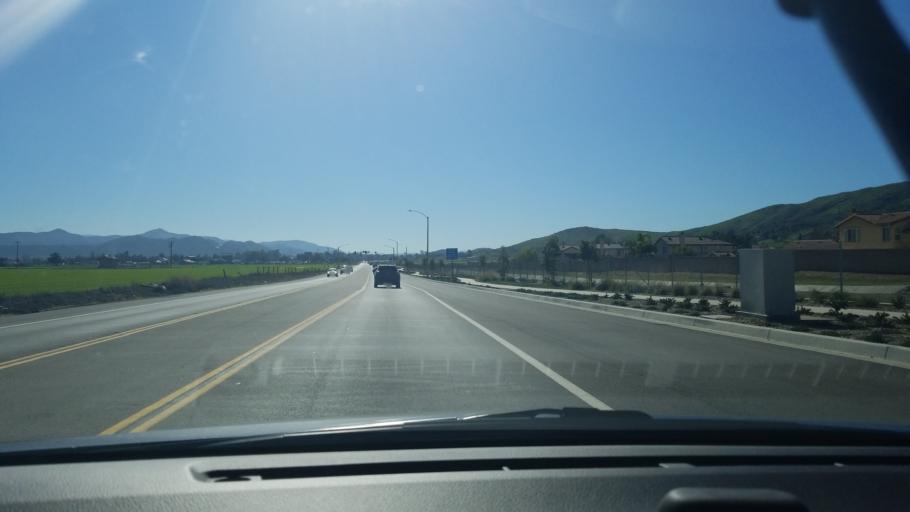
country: US
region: California
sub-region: Riverside County
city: Green Acres
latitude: 33.7323
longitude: -117.0764
